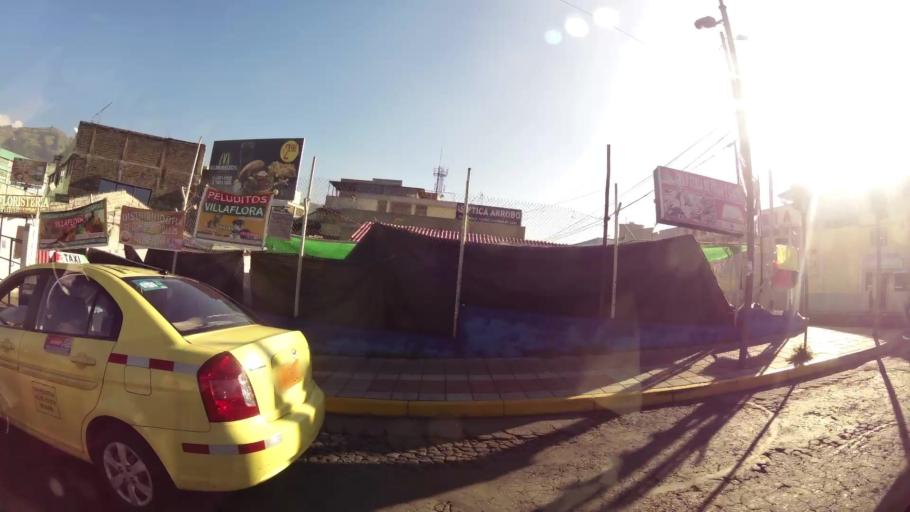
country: EC
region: Pichincha
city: Quito
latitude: -0.2444
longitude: -78.5183
